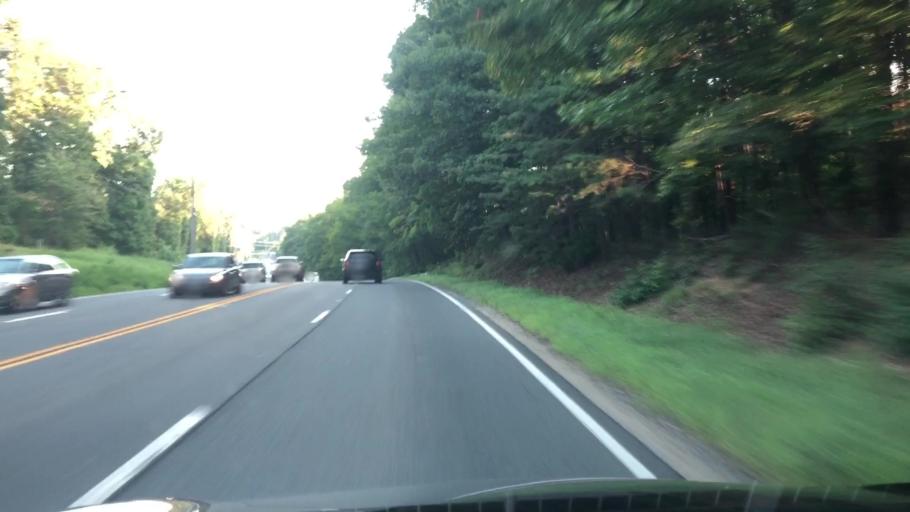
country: US
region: Virginia
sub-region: Stafford County
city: Falmouth
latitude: 38.3572
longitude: -77.4584
